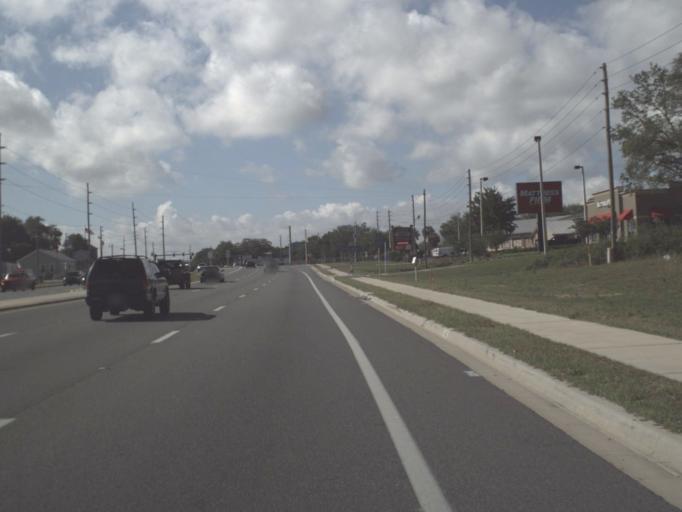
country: US
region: Florida
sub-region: Lake County
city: Fruitland Park
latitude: 28.8461
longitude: -81.8988
